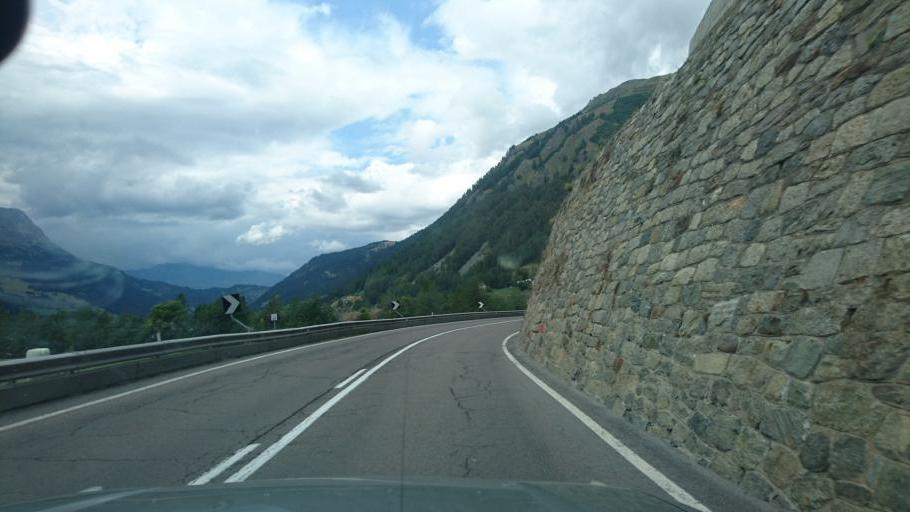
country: IT
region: Trentino-Alto Adige
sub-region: Bolzano
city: Curon Venosta
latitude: 46.8028
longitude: 10.5398
